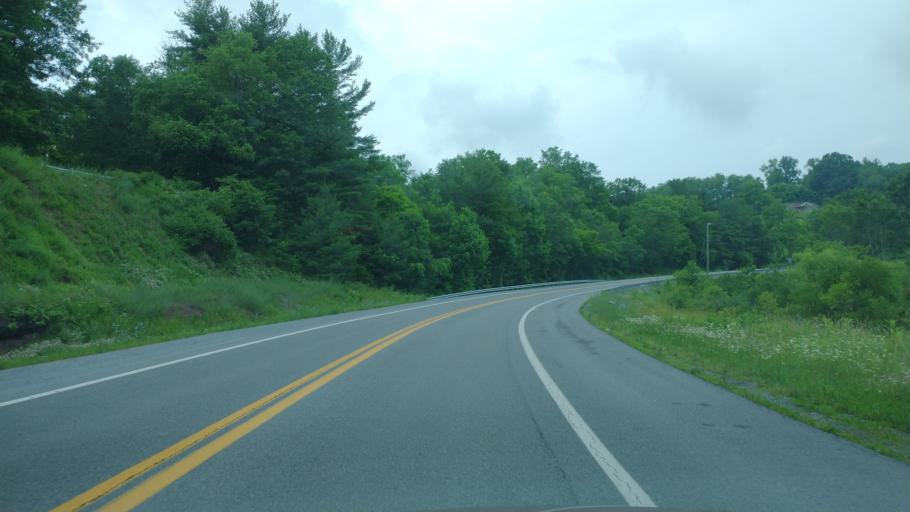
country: US
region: West Virginia
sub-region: Mercer County
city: Athens
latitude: 37.4177
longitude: -81.0592
